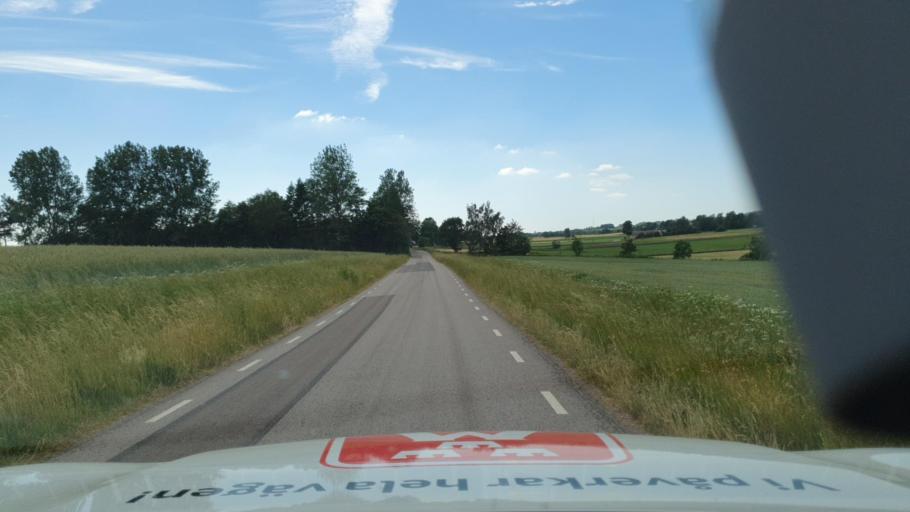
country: SE
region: Skane
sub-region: Sjobo Kommun
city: Sjoebo
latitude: 55.6342
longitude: 13.8181
